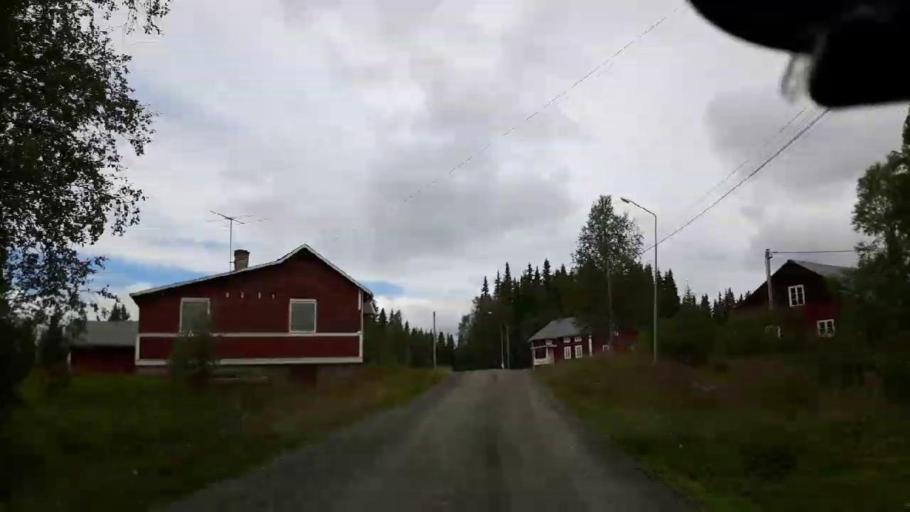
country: SE
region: Jaemtland
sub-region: Krokoms Kommun
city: Valla
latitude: 63.7057
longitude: 13.8675
